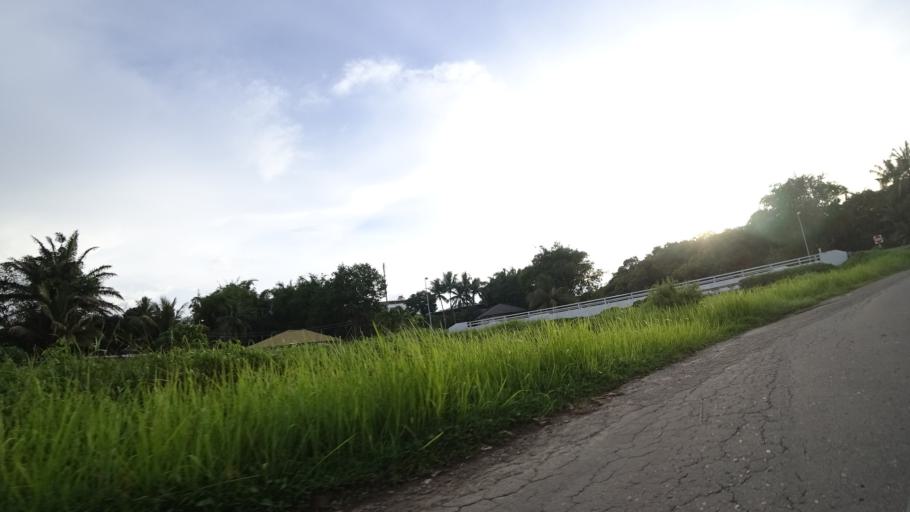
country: BN
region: Brunei and Muara
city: Bandar Seri Begawan
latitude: 4.8650
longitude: 114.8206
